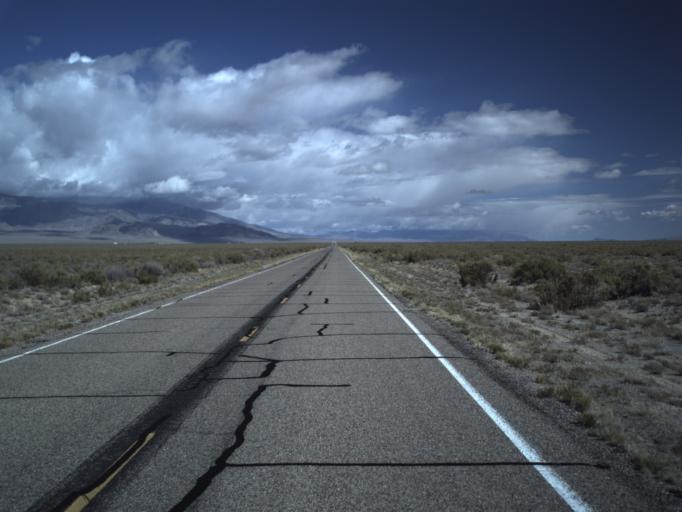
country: US
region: Nevada
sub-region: White Pine County
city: McGill
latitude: 39.0075
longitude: -114.0350
